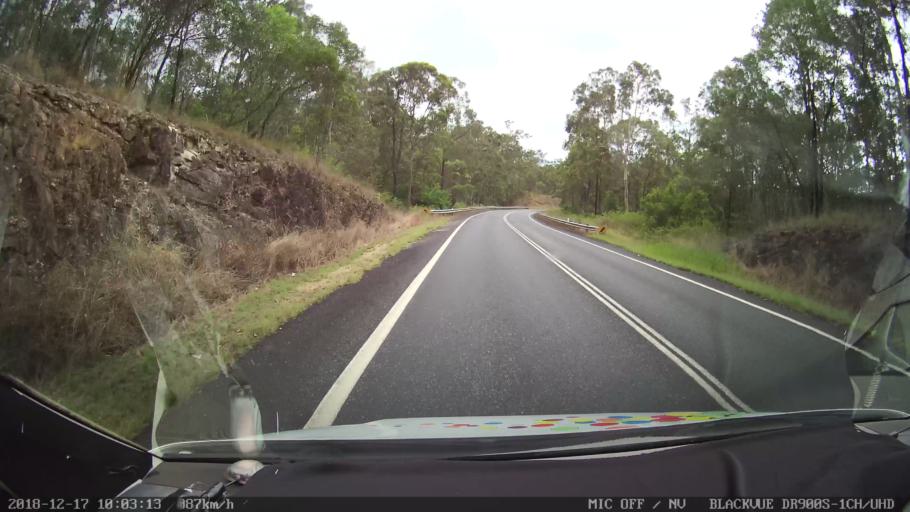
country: AU
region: New South Wales
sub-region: Tenterfield Municipality
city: Carrolls Creek
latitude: -28.8984
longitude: 152.4610
